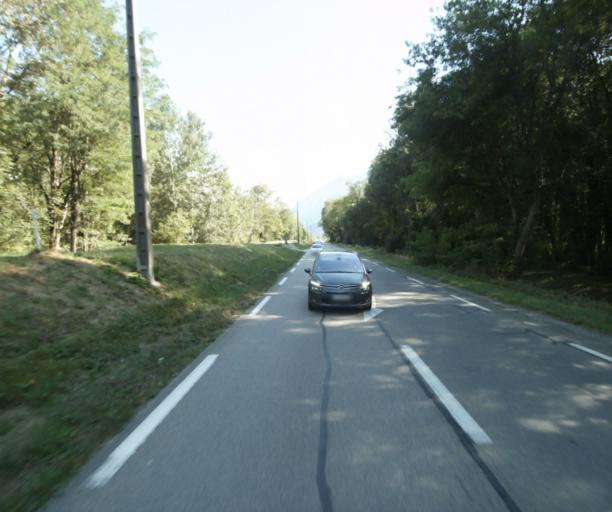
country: FR
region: Rhone-Alpes
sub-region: Departement de l'Isere
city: Veurey-Voroize
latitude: 45.2845
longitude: 5.6169
